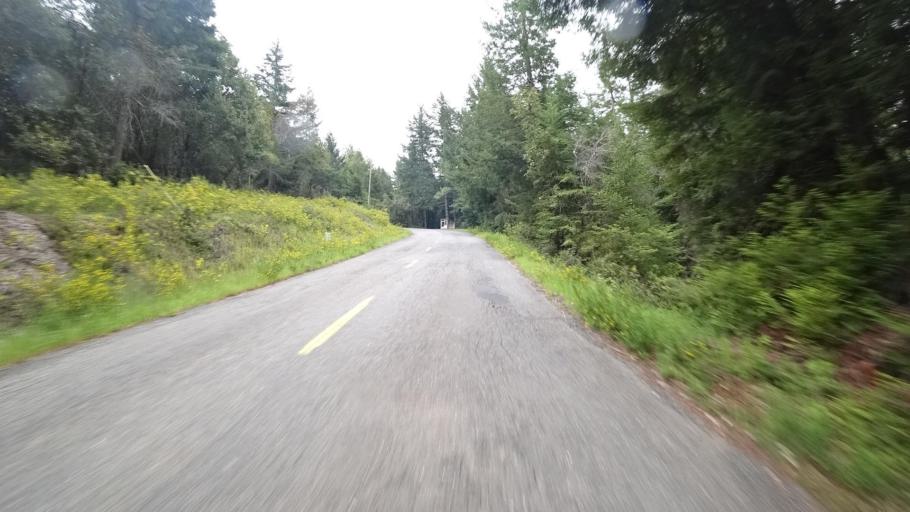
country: US
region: California
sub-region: Humboldt County
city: Redway
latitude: 40.2800
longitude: -123.7971
